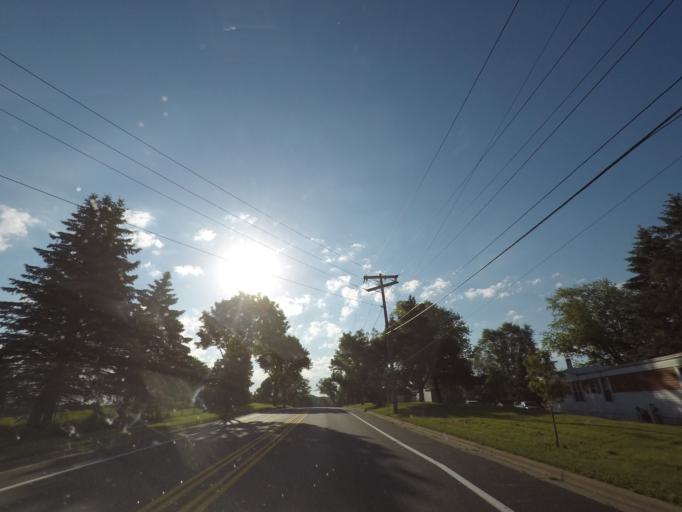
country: US
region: Wisconsin
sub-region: Dane County
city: Monona
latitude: 43.0328
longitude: -89.3596
